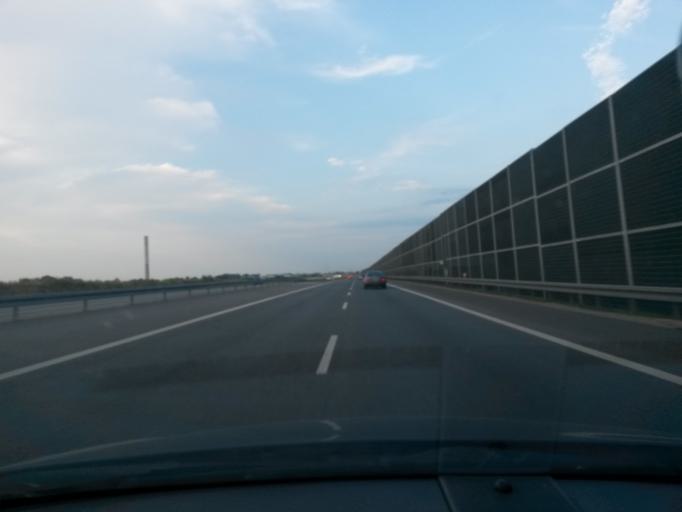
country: PL
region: Masovian Voivodeship
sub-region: Powiat pruszkowski
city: Brwinow
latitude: 52.1591
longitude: 20.7084
